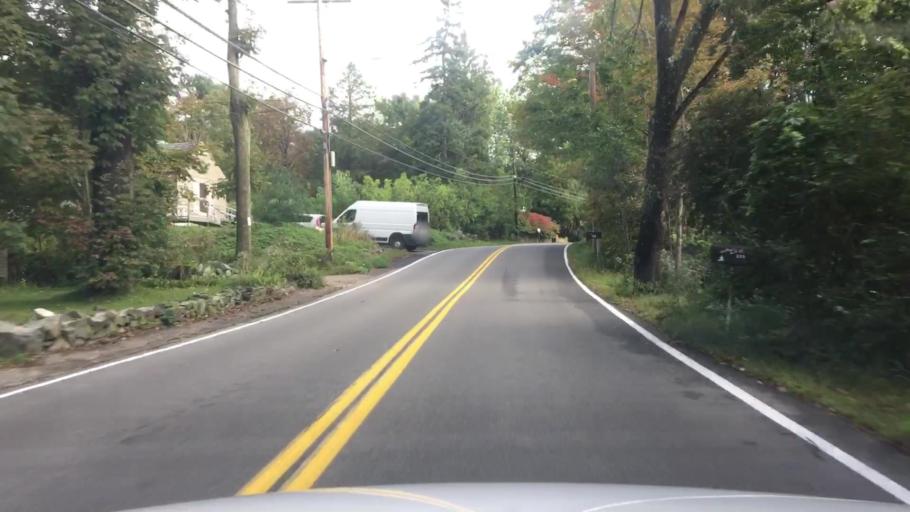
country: US
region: Maine
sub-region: York County
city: Kittery Point
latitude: 43.0970
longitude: -70.6777
